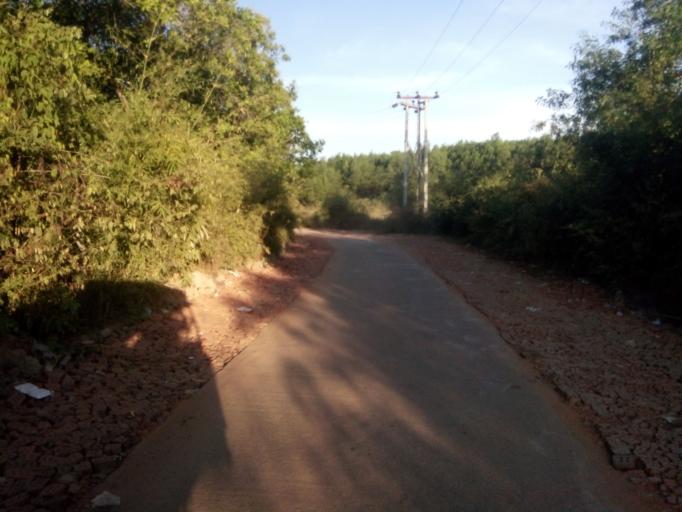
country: MM
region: Bago
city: Thanatpin
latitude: 17.2714
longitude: 96.2306
